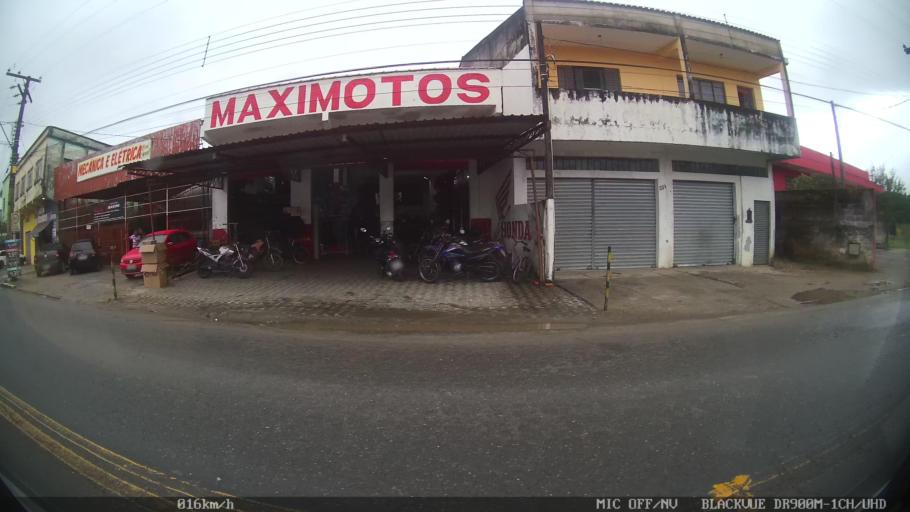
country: BR
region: Sao Paulo
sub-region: Juquia
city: Juquia
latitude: -24.3267
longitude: -47.6317
